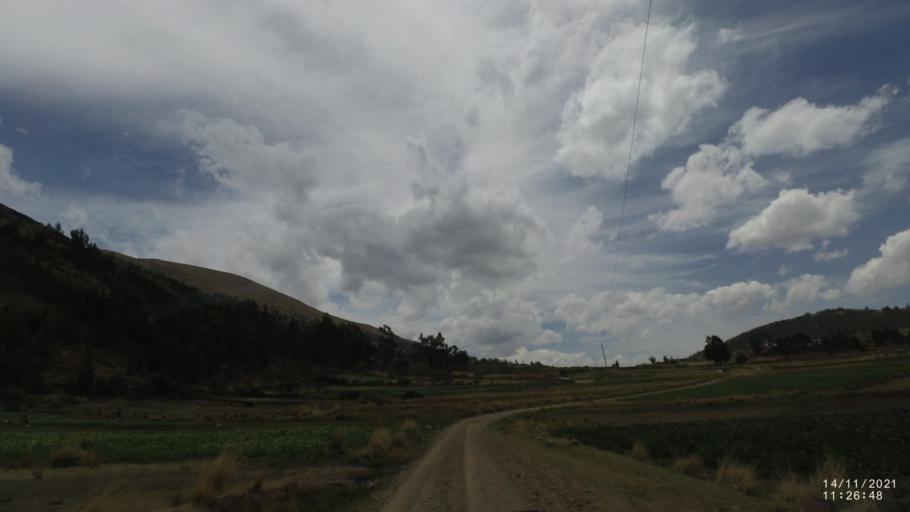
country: BO
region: Cochabamba
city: Cochabamba
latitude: -17.3384
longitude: -66.0169
